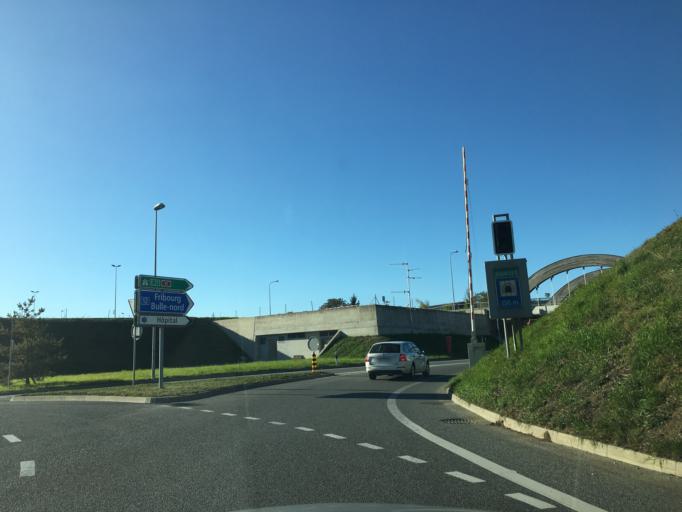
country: CH
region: Fribourg
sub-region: Gruyere District
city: Bulle
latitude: 46.6174
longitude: 7.0459
